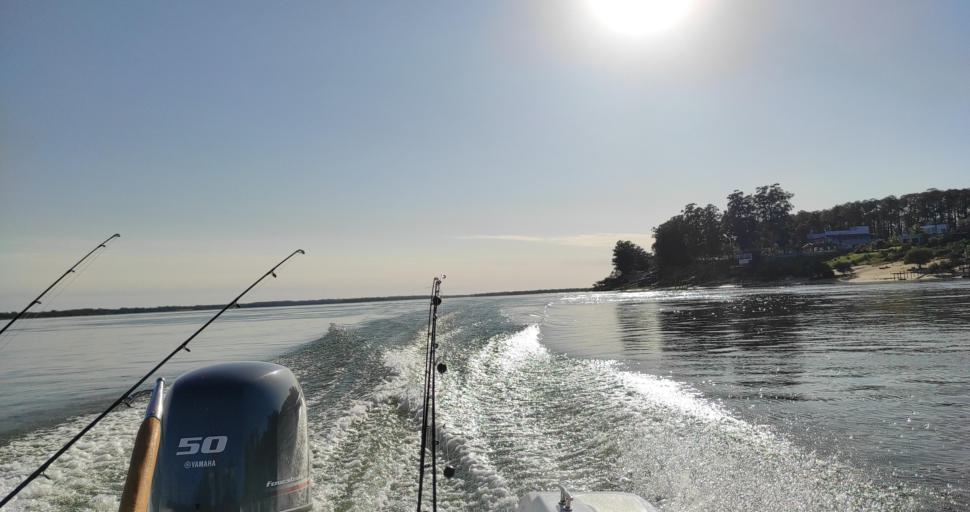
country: AR
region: Corrientes
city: Ituzaingo
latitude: -27.5986
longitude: -56.8166
